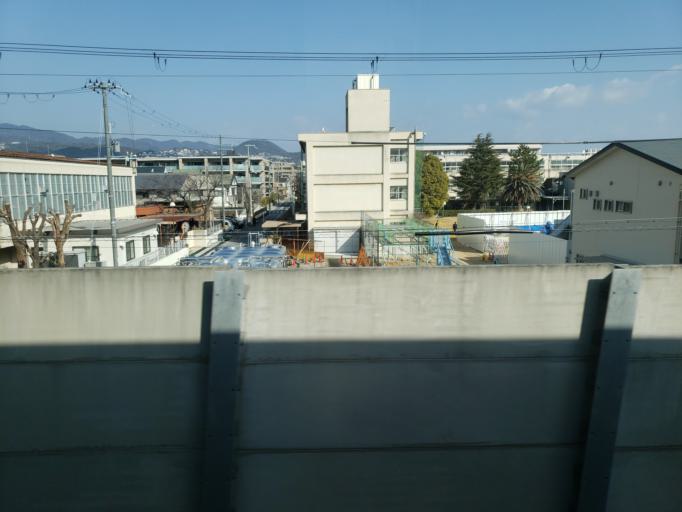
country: JP
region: Hyogo
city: Nishinomiya-hama
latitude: 34.7393
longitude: 135.3337
